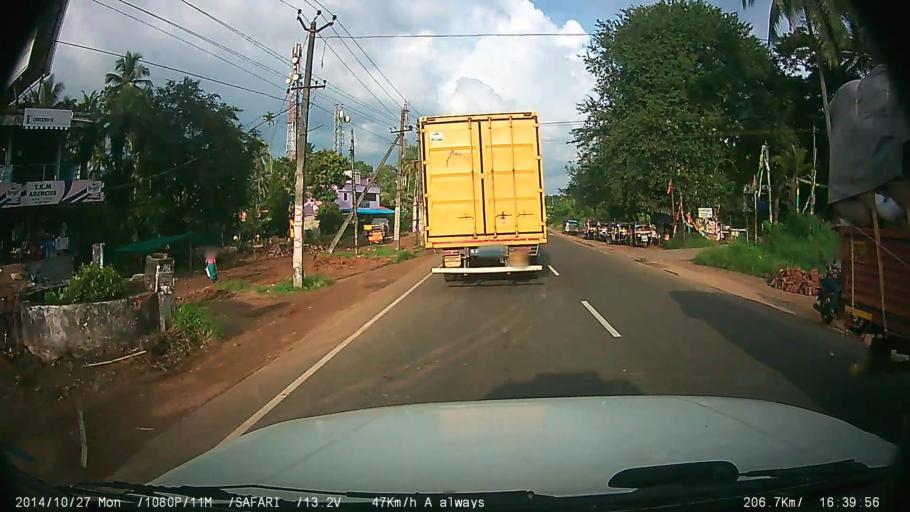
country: IN
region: Kerala
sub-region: Thrissur District
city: Trichur
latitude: 10.5498
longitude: 76.3057
